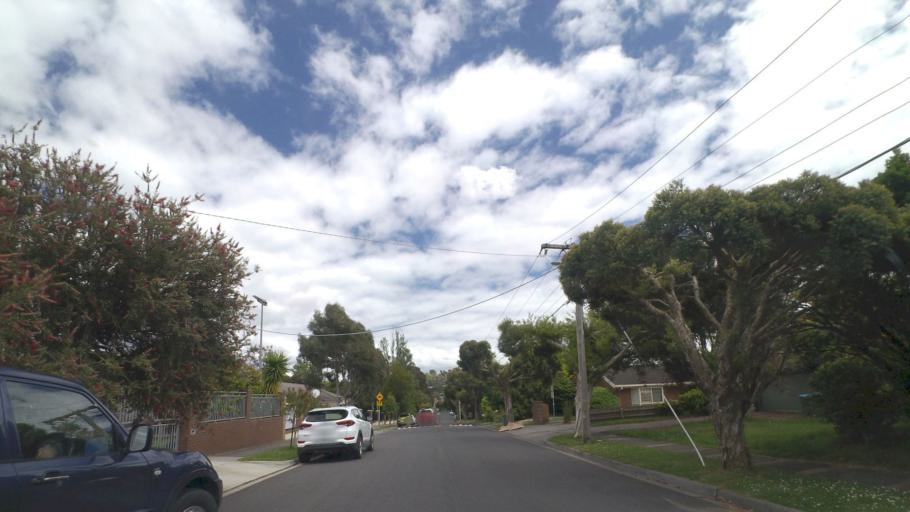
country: AU
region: Victoria
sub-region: Maroondah
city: Croydon North
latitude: -37.7951
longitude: 145.2899
